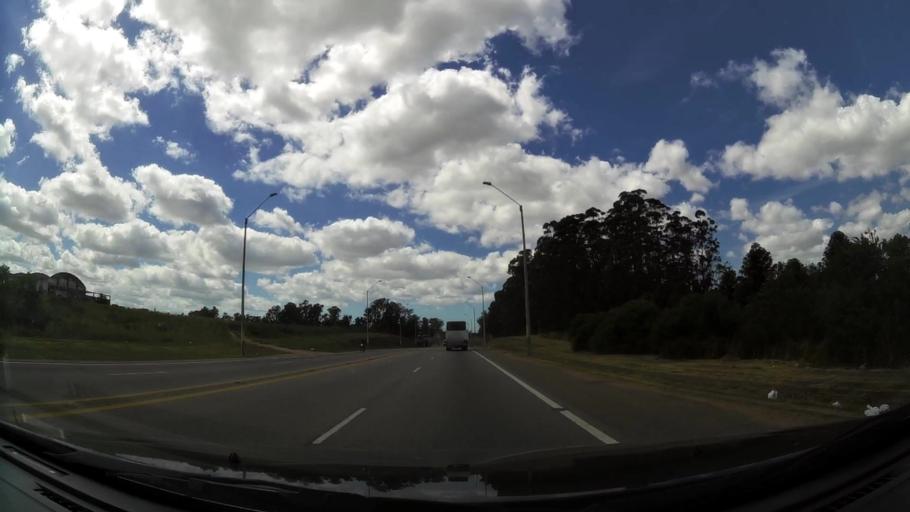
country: UY
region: Canelones
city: Colonia Nicolich
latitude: -34.8057
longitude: -56.0491
